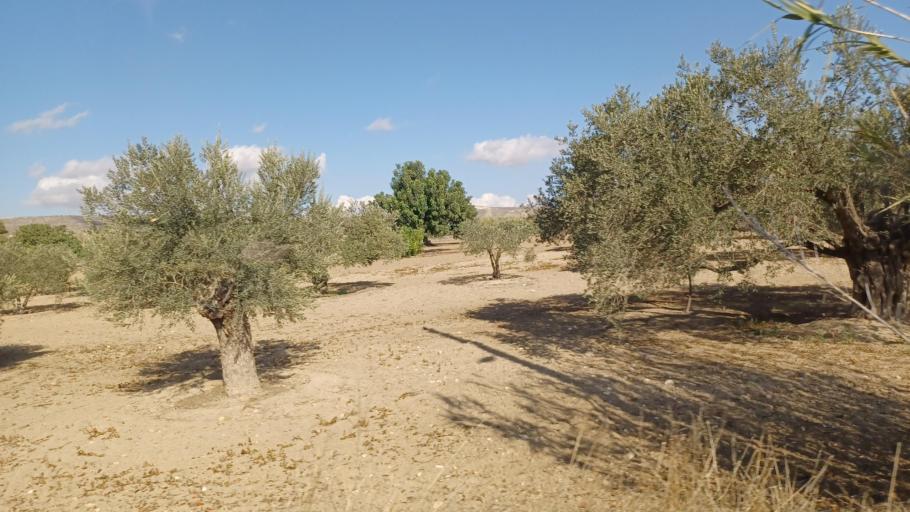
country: CY
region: Larnaka
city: Troulloi
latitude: 35.0316
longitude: 33.6099
